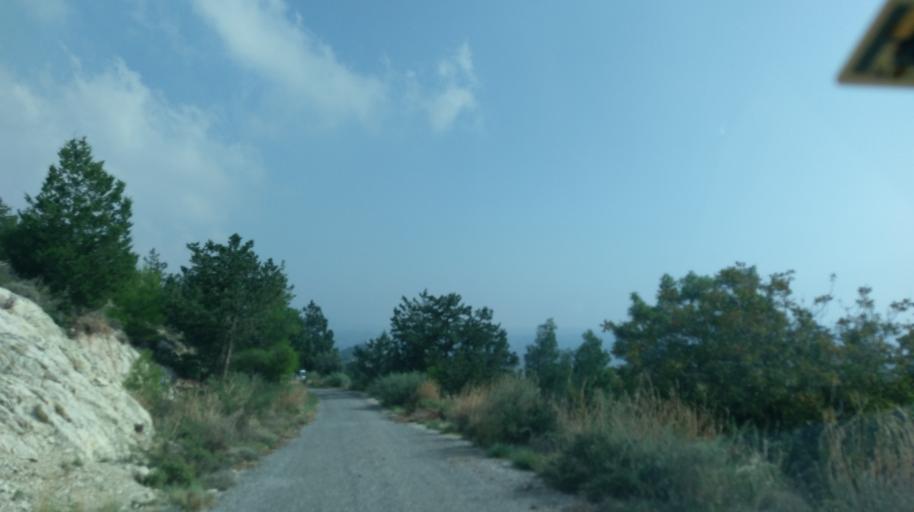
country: CY
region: Ammochostos
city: Lefkonoiko
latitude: 35.3159
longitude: 33.6187
